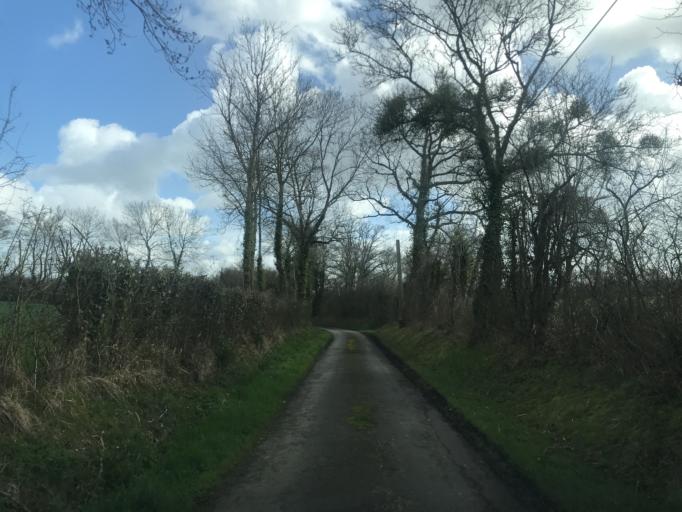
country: FR
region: Lower Normandy
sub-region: Departement du Calvados
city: Dives-sur-Mer
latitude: 49.2671
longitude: -0.0980
